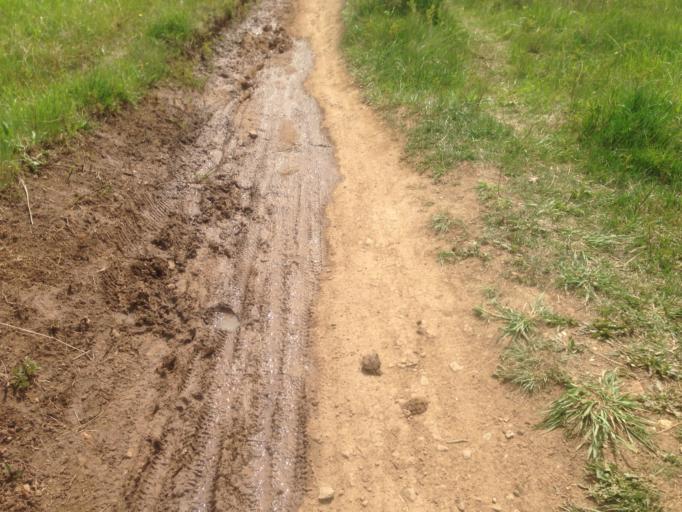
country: US
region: Colorado
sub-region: Boulder County
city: Superior
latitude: 39.9469
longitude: -105.2350
